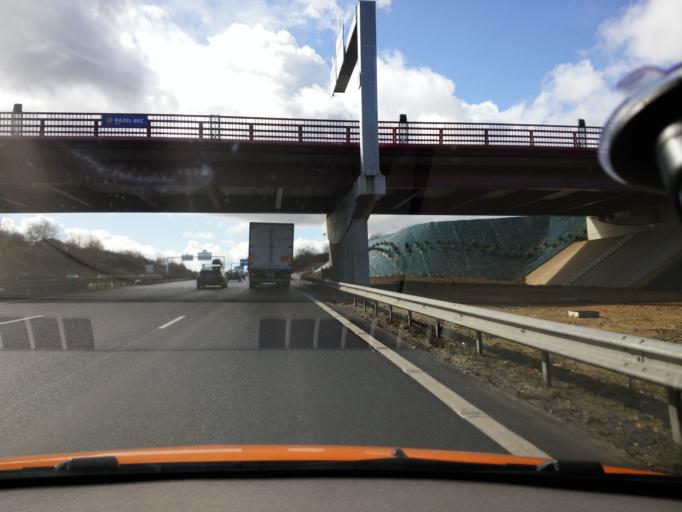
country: FR
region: Ile-de-France
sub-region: Departement de l'Essonne
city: Villejust
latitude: 48.6920
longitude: 2.2252
